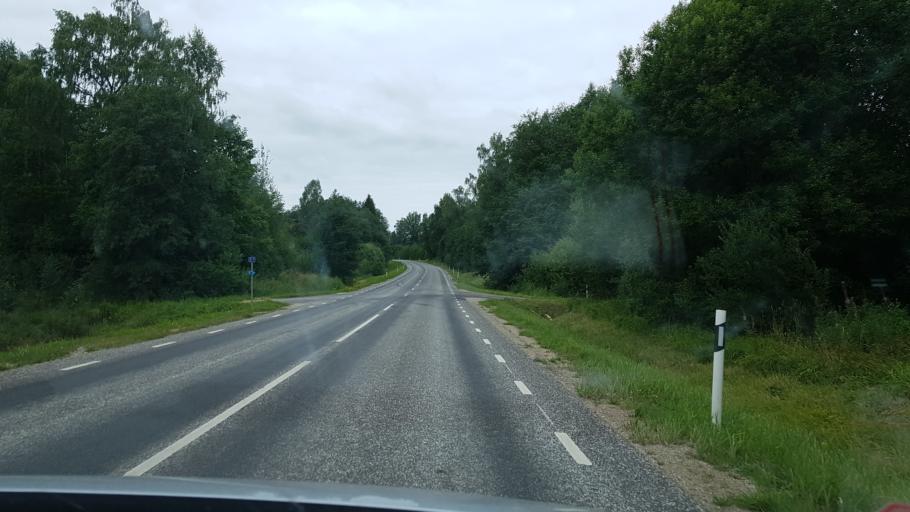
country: EE
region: Vorumaa
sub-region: Antsla vald
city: Vana-Antsla
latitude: 58.0123
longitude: 26.5964
